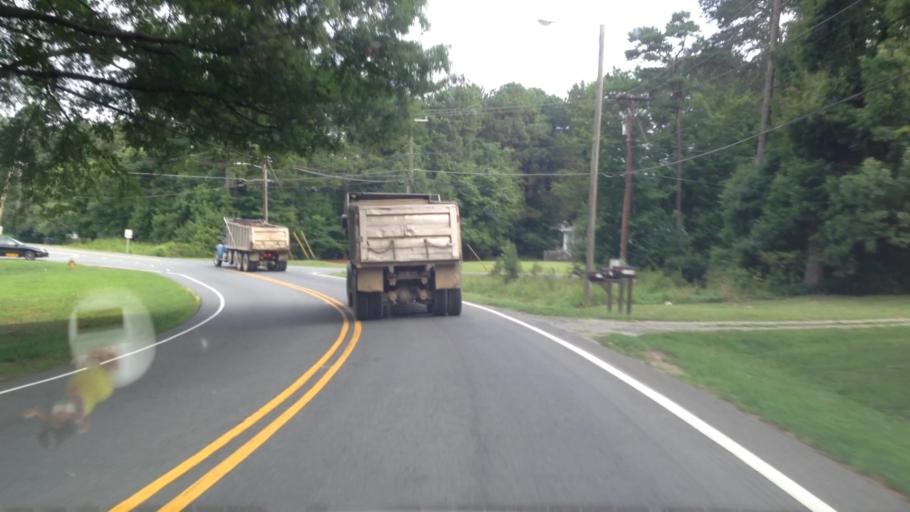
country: US
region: North Carolina
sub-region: Forsyth County
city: Walkertown
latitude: 36.1841
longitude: -80.2015
